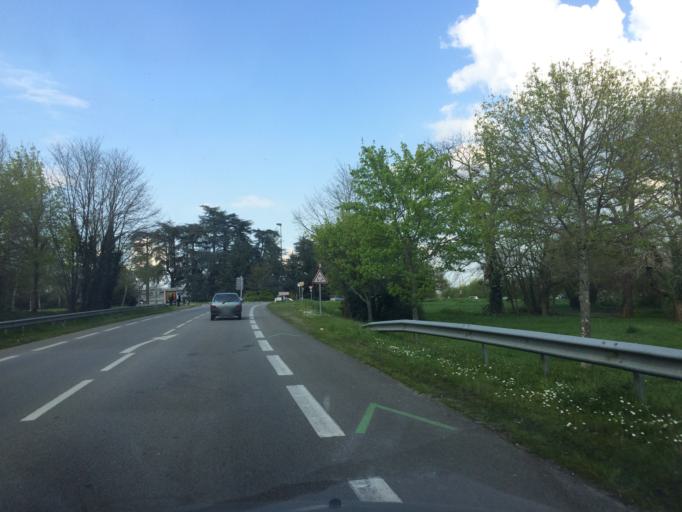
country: FR
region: Pays de la Loire
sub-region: Departement de la Loire-Atlantique
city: Carquefou
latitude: 47.2975
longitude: -1.4999
